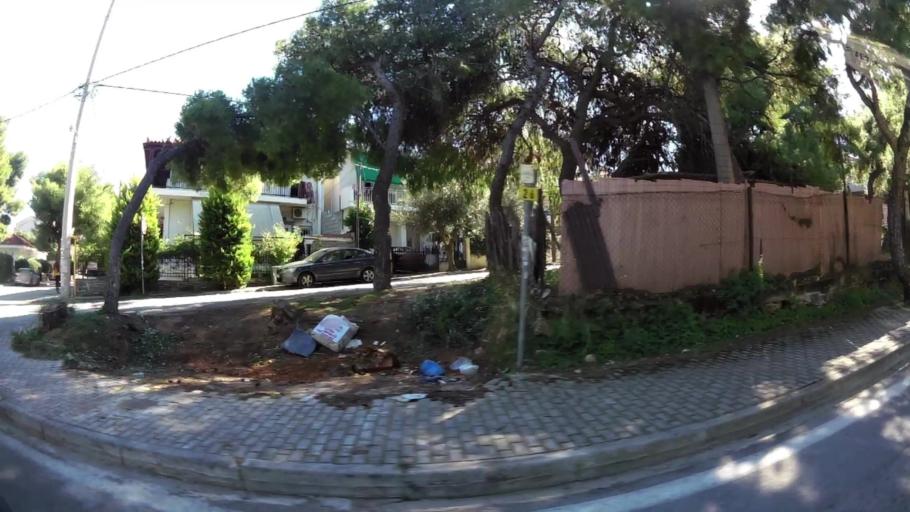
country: GR
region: Attica
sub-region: Nomarchia Athinas
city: Nea Erythraia
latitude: 38.0944
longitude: 23.8062
